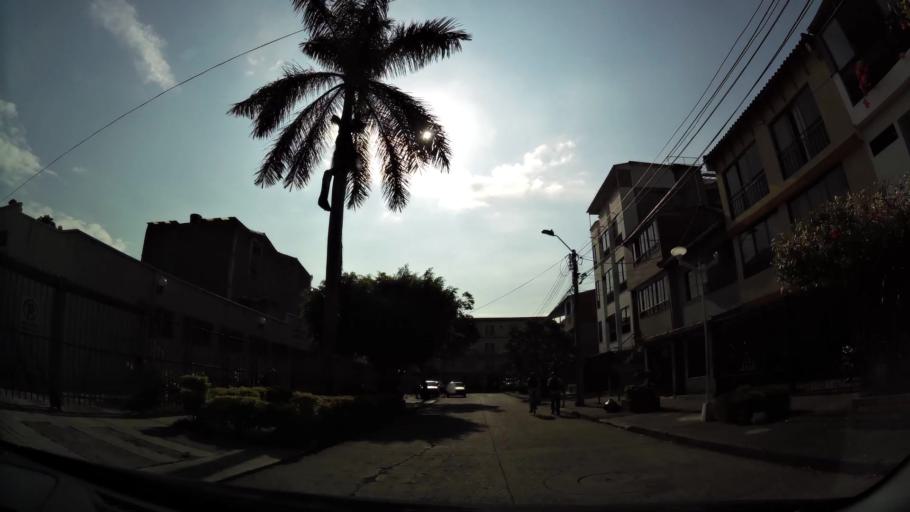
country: CO
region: Valle del Cauca
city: Cali
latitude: 3.4187
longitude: -76.5330
